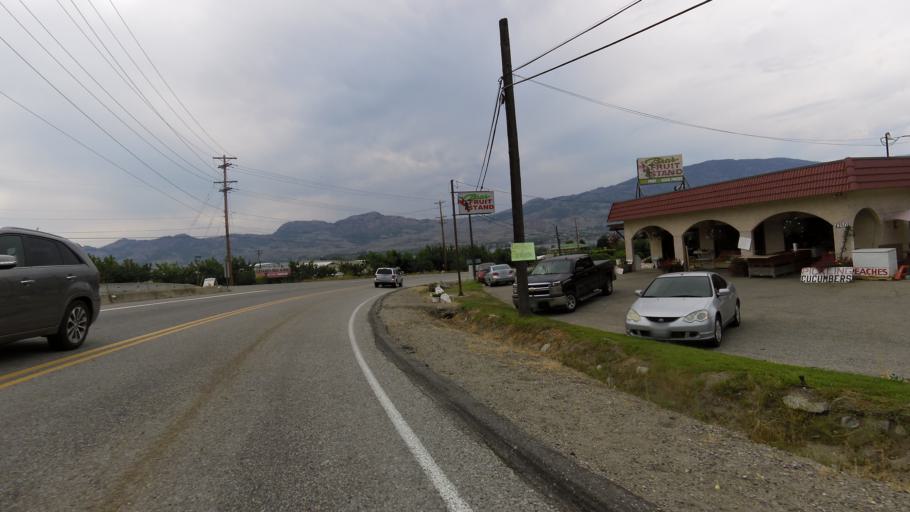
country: CA
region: British Columbia
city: Osoyoos
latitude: 49.0282
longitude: -119.4317
